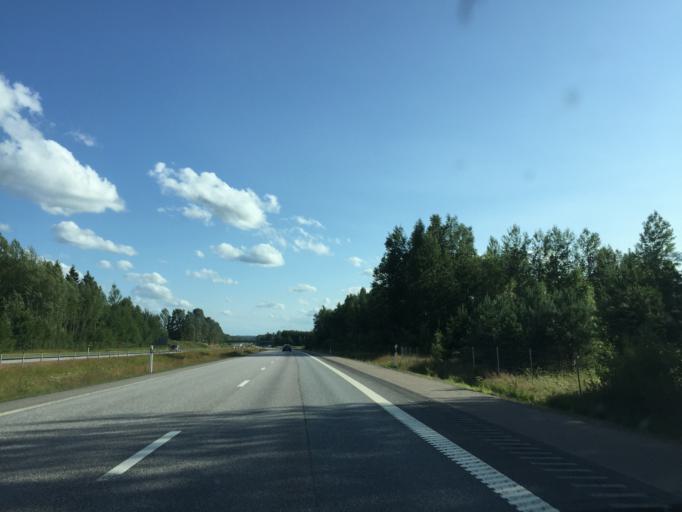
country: SE
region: OErebro
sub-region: Kumla Kommun
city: Kumla
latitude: 59.1307
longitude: 15.0757
